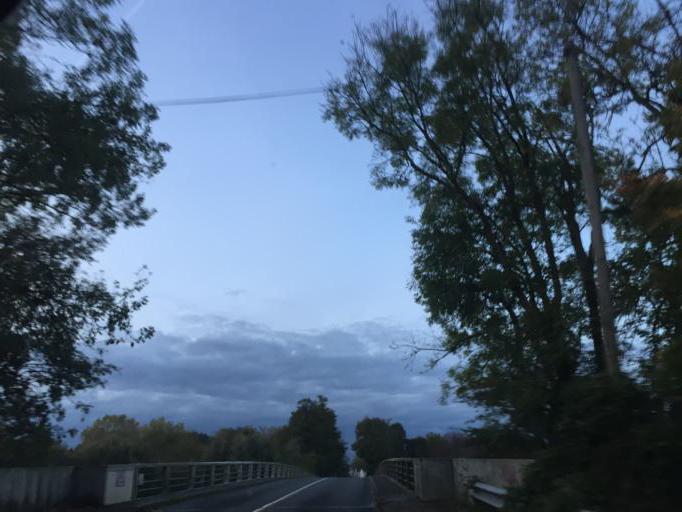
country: FR
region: Ile-de-France
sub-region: Departement de Seine-et-Marne
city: Annet-sur-Marne
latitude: 48.9210
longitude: 2.7253
